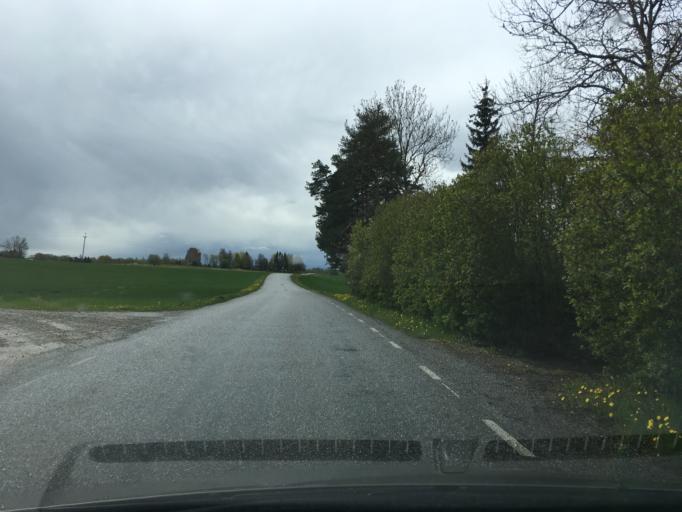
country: EE
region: Harju
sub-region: Joelaehtme vald
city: Loo
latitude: 59.4244
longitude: 24.9884
